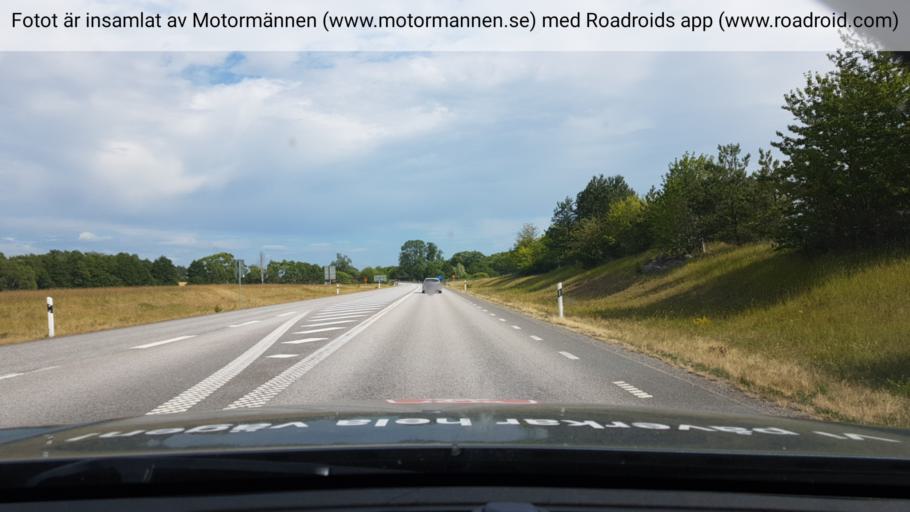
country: SE
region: Uppsala
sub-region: Enkopings Kommun
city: Orsundsbro
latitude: 59.8556
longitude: 17.4302
